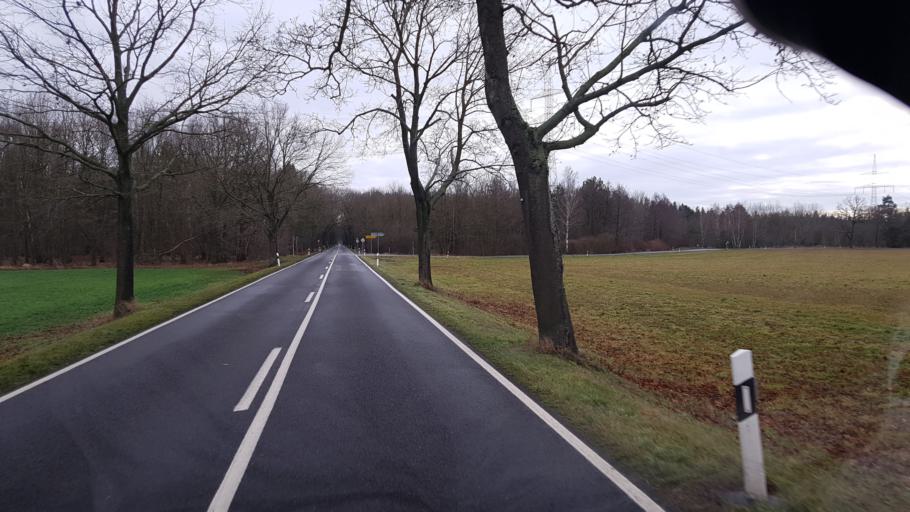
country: DE
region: Brandenburg
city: Altdobern
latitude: 51.6702
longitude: 14.0333
